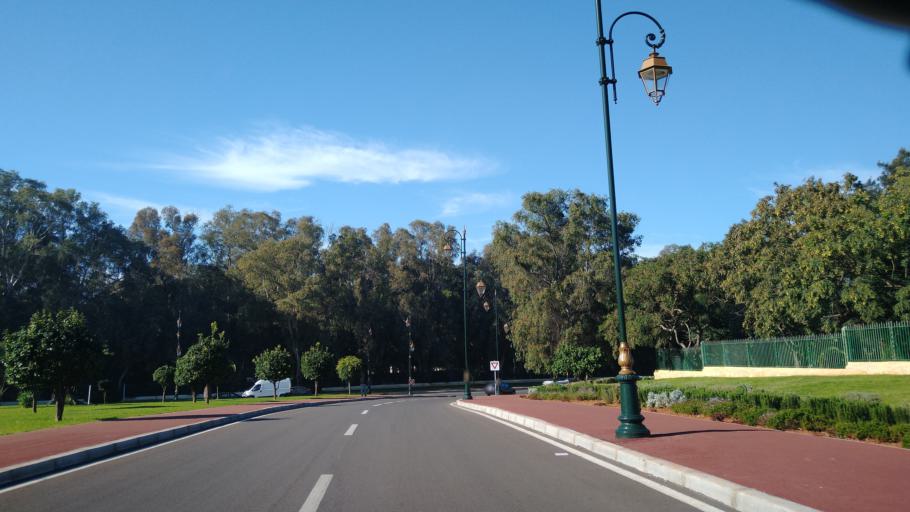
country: MA
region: Rabat-Sale-Zemmour-Zaer
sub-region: Rabat
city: Rabat
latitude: 33.9941
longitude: -6.8373
